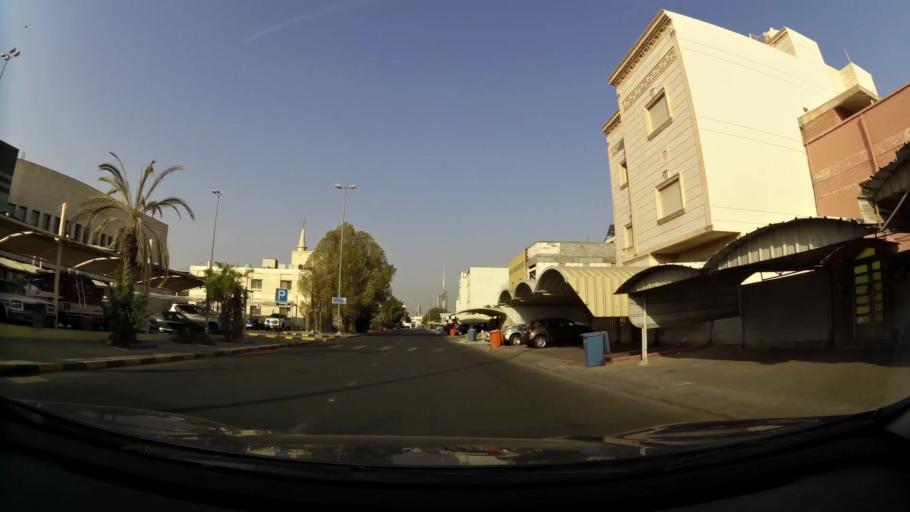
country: KW
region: Al Asimah
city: Ad Dasmah
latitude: 29.3665
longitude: 48.0015
